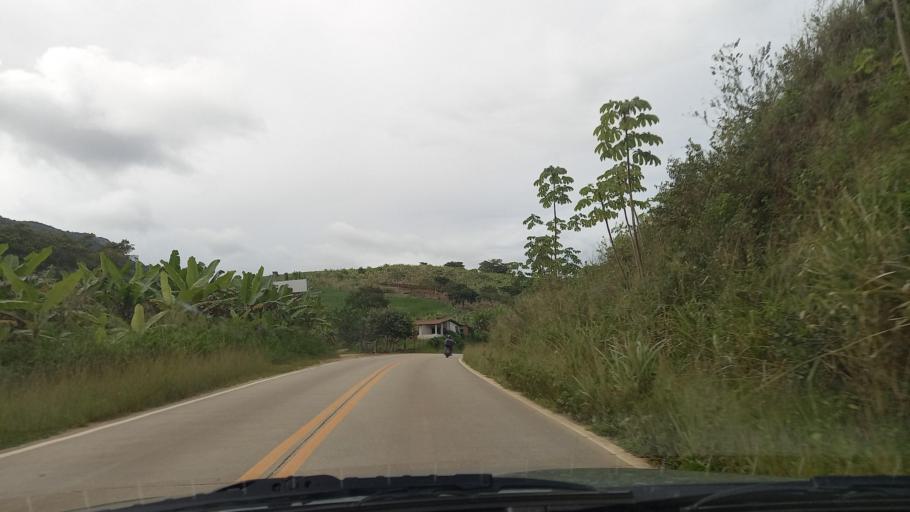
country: BR
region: Pernambuco
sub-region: Maraial
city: Maraial
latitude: -8.7554
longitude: -35.8475
